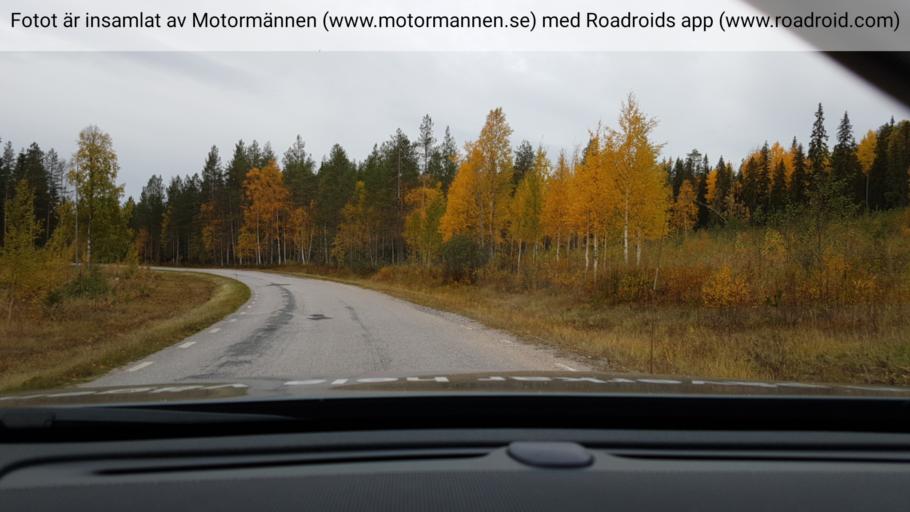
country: SE
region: Norrbotten
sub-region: Overkalix Kommun
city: OEverkalix
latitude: 66.2380
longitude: 22.9736
